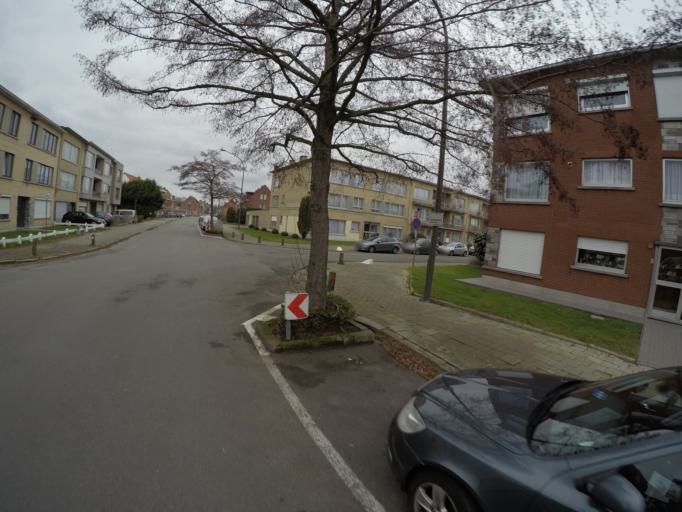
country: BE
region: Flanders
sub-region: Provincie Antwerpen
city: Zwijndrecht
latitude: 51.2168
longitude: 4.3362
